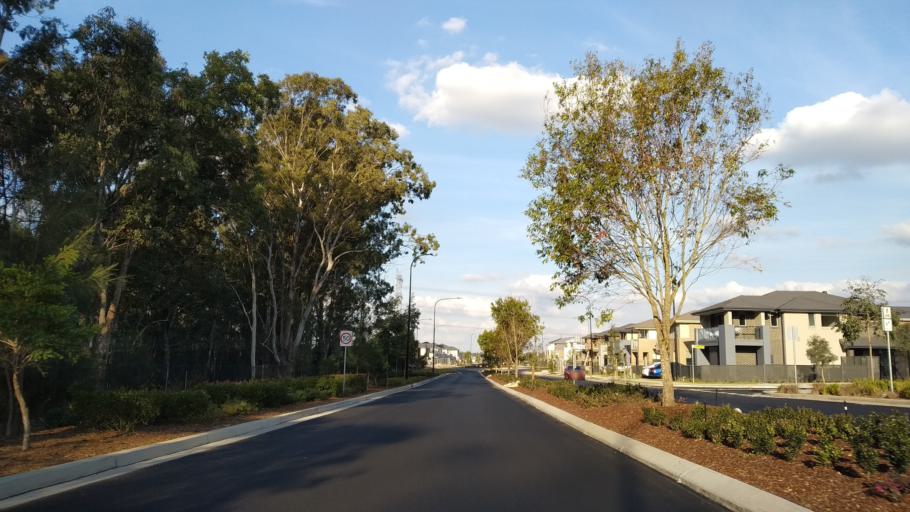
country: AU
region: New South Wales
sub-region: Penrith Municipality
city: Werrington County
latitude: -33.7328
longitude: 150.7477
